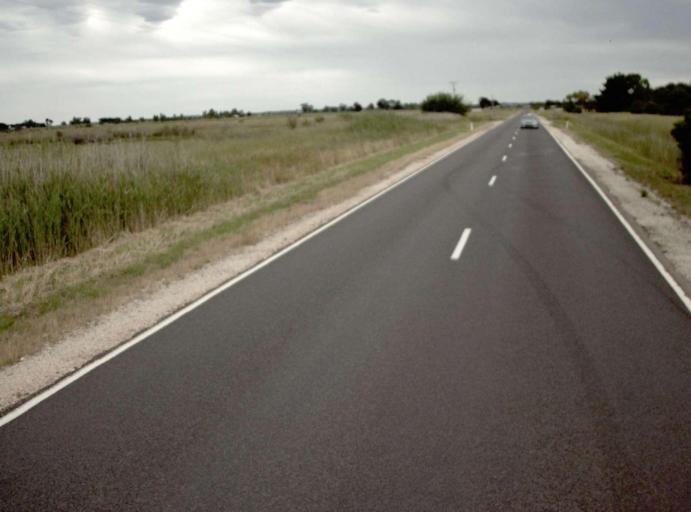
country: AU
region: Victoria
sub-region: Wellington
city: Sale
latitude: -38.0644
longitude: 147.1468
